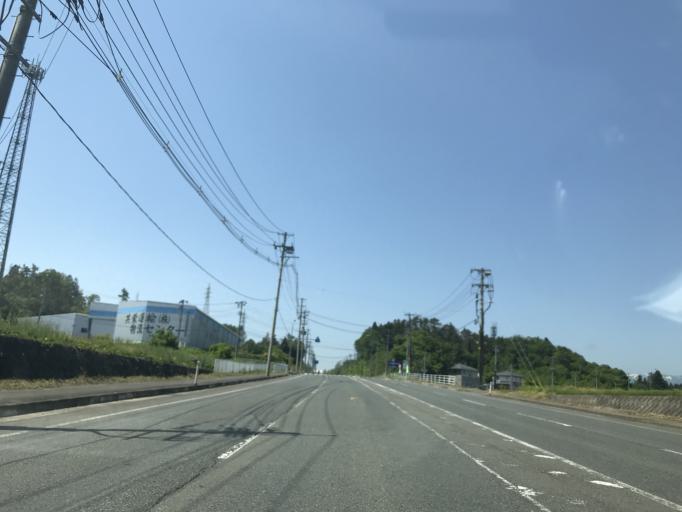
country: JP
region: Iwate
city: Kitakami
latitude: 39.2200
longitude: 141.0882
